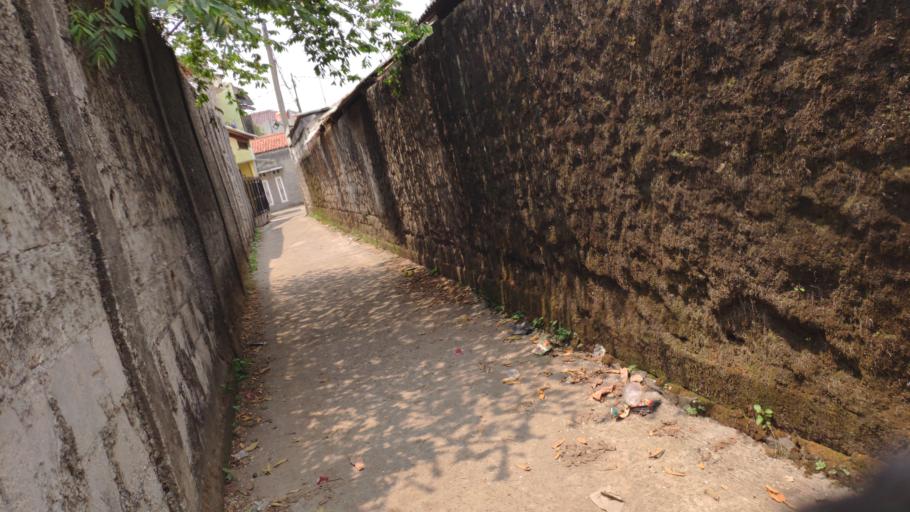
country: ID
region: West Java
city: Pamulang
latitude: -6.3309
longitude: 106.7934
